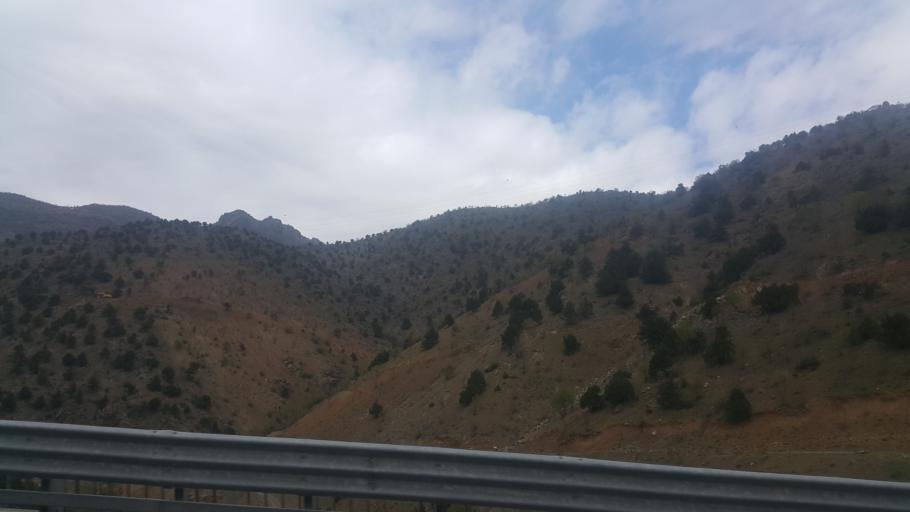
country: TR
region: Nigde
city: Ciftehan
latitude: 37.5408
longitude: 34.7904
